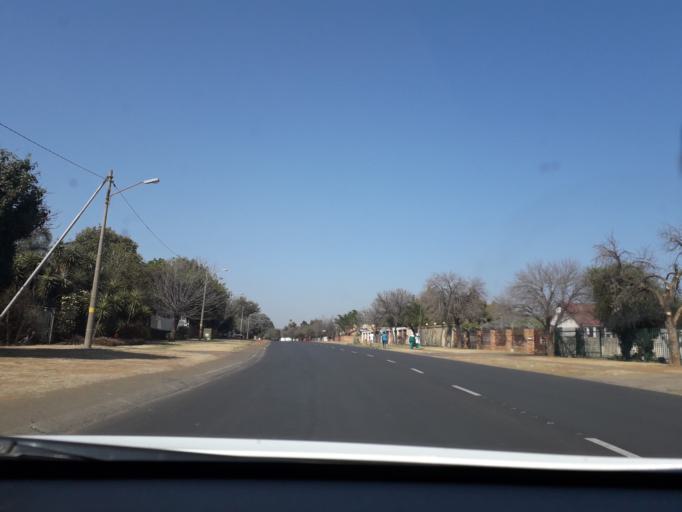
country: ZA
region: Gauteng
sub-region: City of Johannesburg Metropolitan Municipality
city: Modderfontein
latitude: -26.0942
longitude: 28.2424
